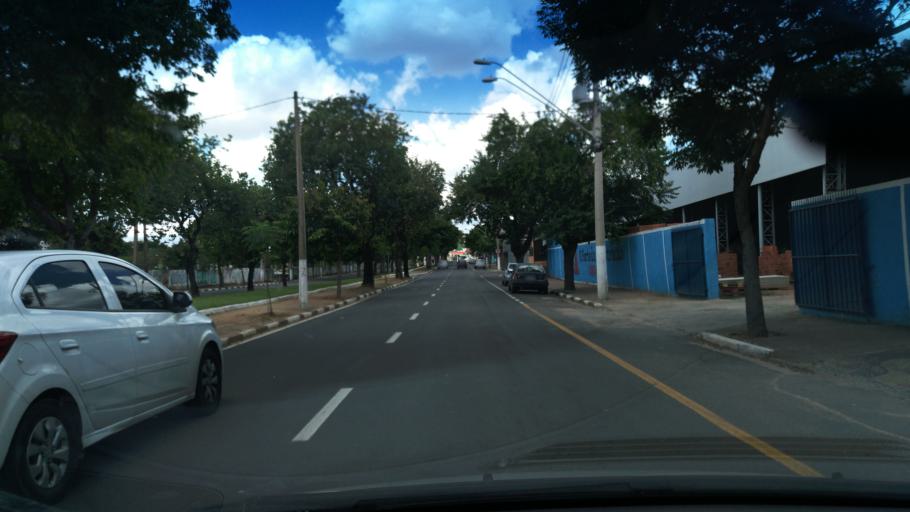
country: BR
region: Sao Paulo
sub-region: Valinhos
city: Valinhos
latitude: -22.9809
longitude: -46.9905
